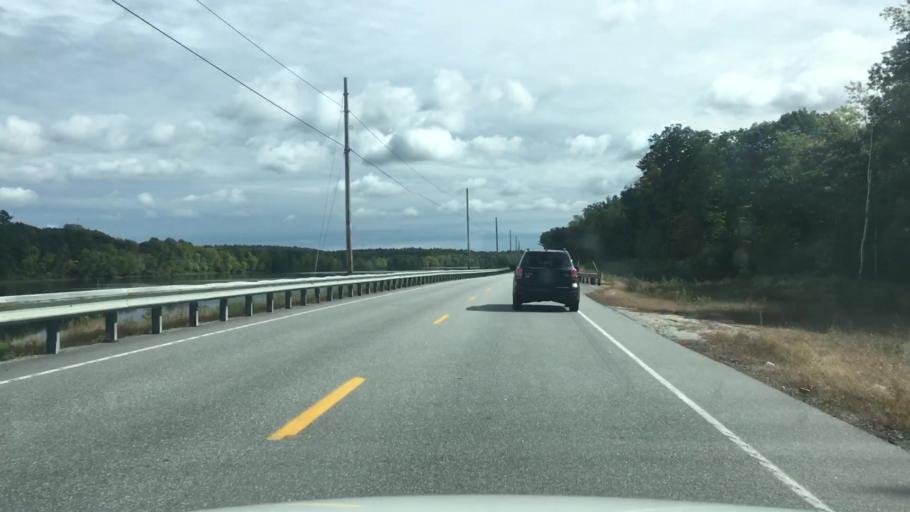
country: US
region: Maine
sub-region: Androscoggin County
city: Lisbon
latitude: 44.0045
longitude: -70.1591
